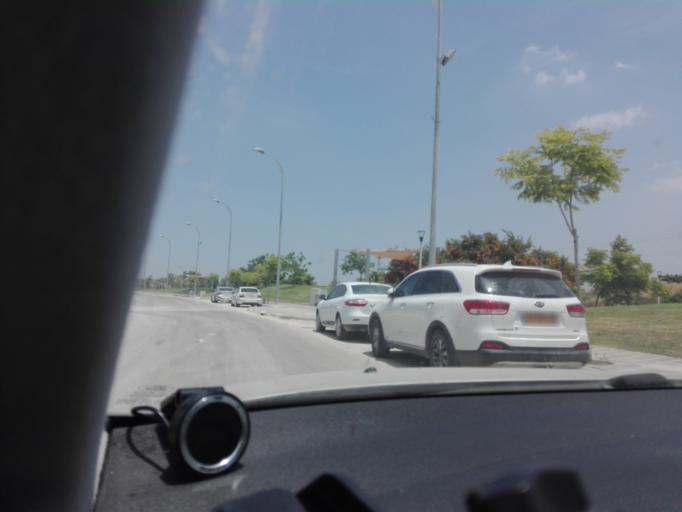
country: IL
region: Central District
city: Bene 'Ayish
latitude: 31.7393
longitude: 34.7454
